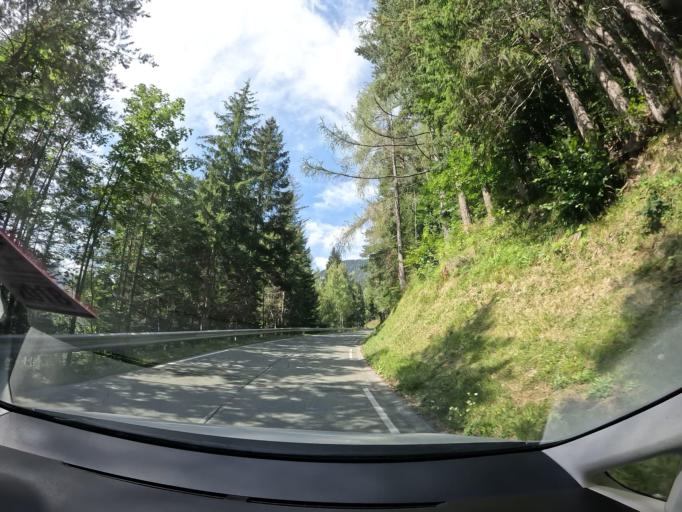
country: AT
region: Carinthia
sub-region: Politischer Bezirk Feldkirchen
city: Glanegg
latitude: 46.7370
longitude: 14.2111
